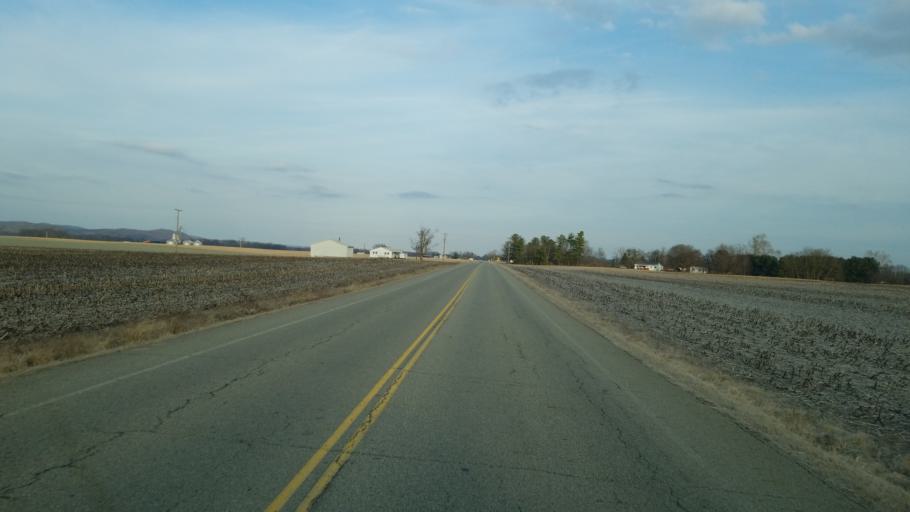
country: US
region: Ohio
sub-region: Ross County
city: Chillicothe
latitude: 39.2458
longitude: -82.8687
